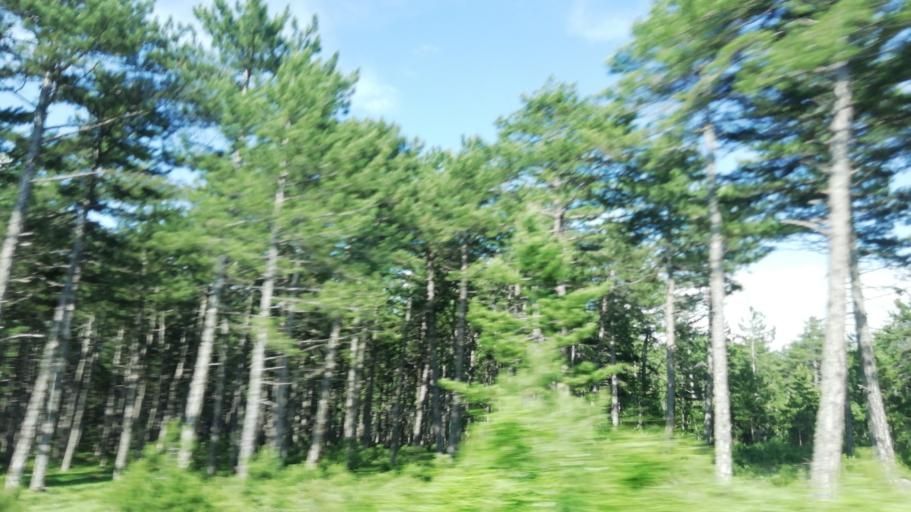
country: TR
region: Karabuk
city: Karabuk
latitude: 41.1137
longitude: 32.6065
